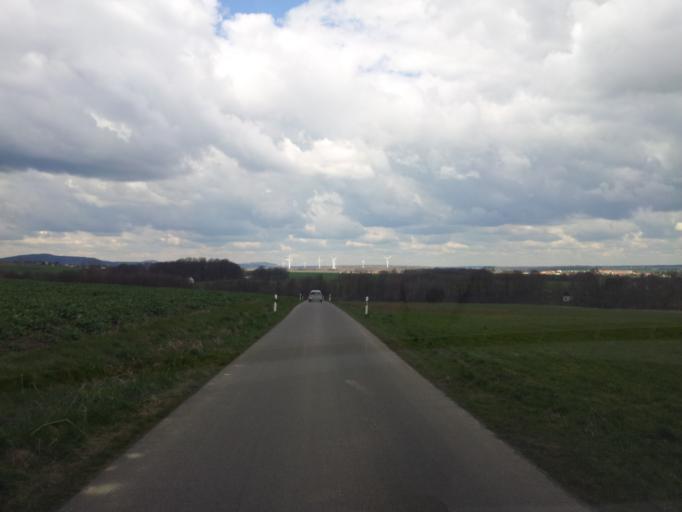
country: DE
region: Saxony
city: Panschwitz-Kuckau
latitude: 51.2109
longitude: 14.2101
